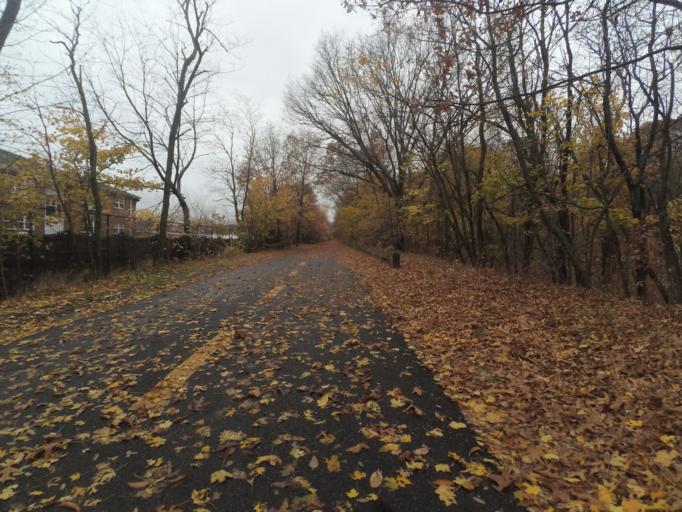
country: US
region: Massachusetts
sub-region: Middlesex County
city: Arlington
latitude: 42.4231
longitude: -71.1701
